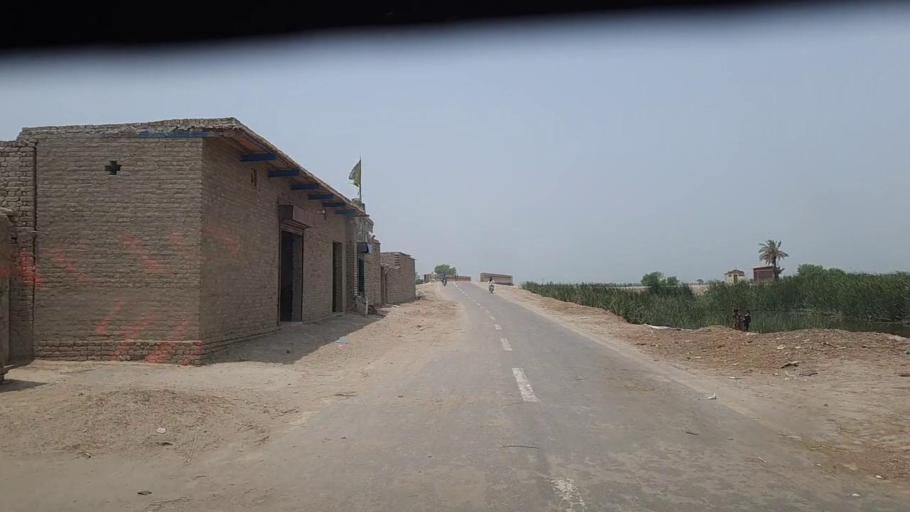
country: PK
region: Sindh
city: Sita Road
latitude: 27.0399
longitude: 67.8970
